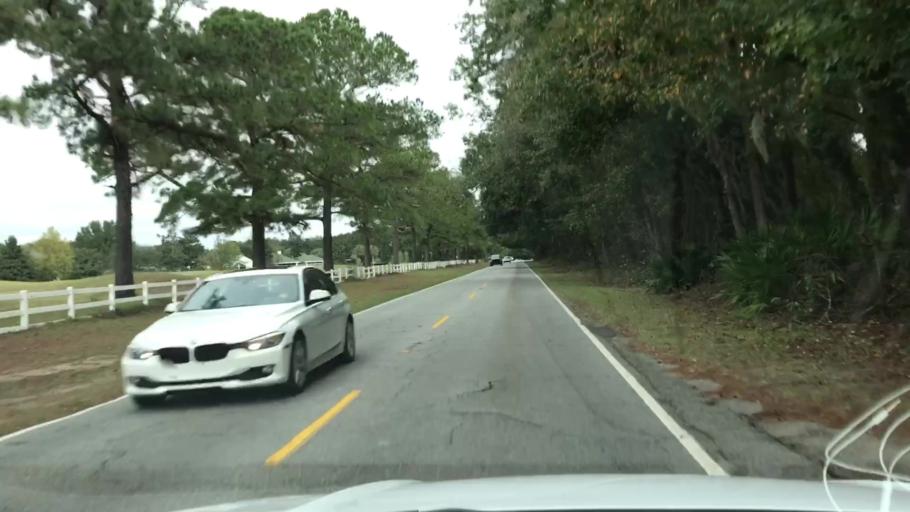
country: US
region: South Carolina
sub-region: Beaufort County
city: Bluffton
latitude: 32.2676
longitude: -80.8802
